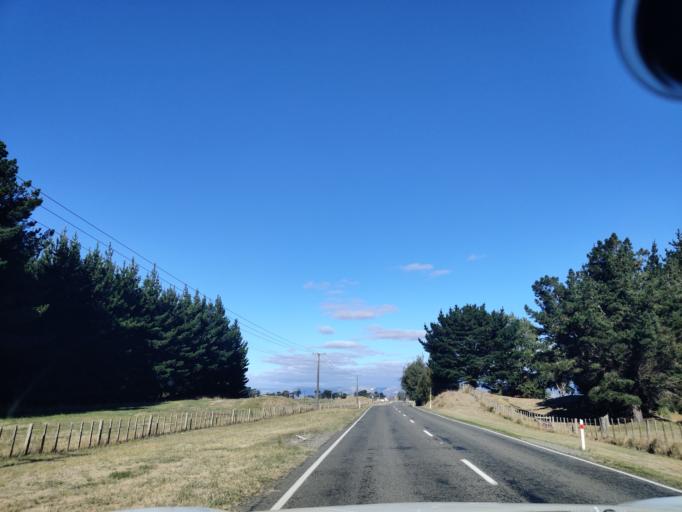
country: NZ
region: Manawatu-Wanganui
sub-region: Horowhenua District
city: Foxton
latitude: -40.4030
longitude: 175.3653
